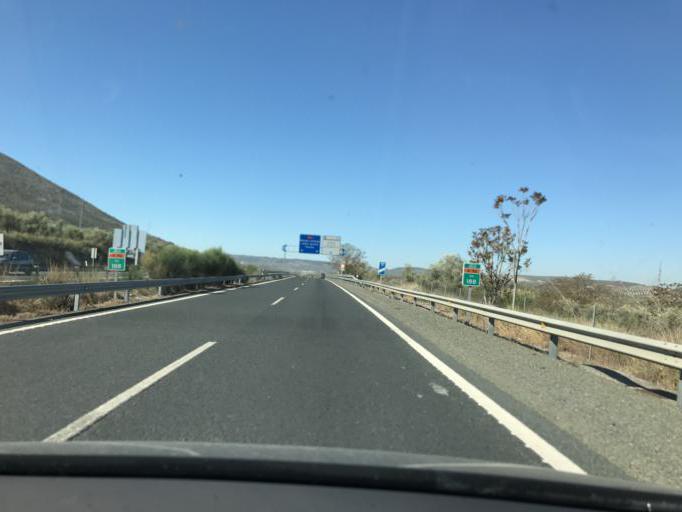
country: ES
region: Andalusia
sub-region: Provincia de Granada
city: Loja
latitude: 37.1651
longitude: -4.1829
